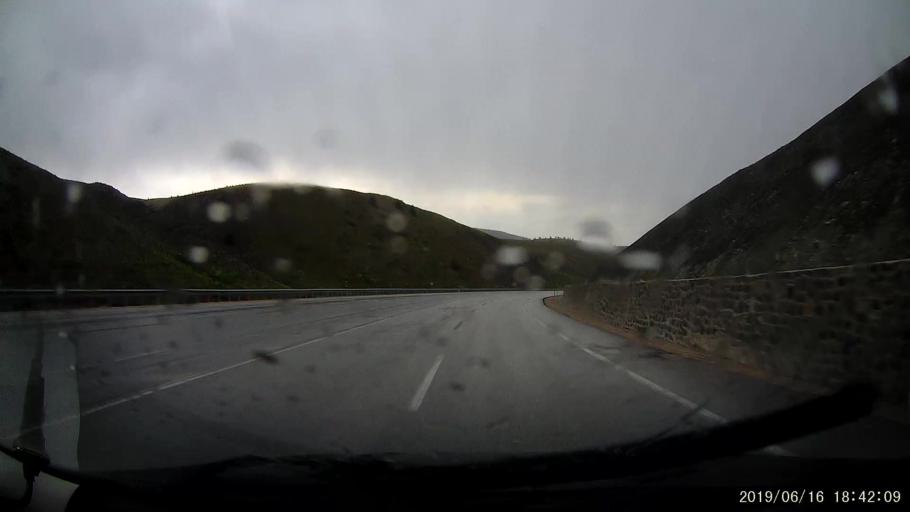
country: TR
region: Erzincan
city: Doganbeyli
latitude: 39.8708
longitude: 39.1154
